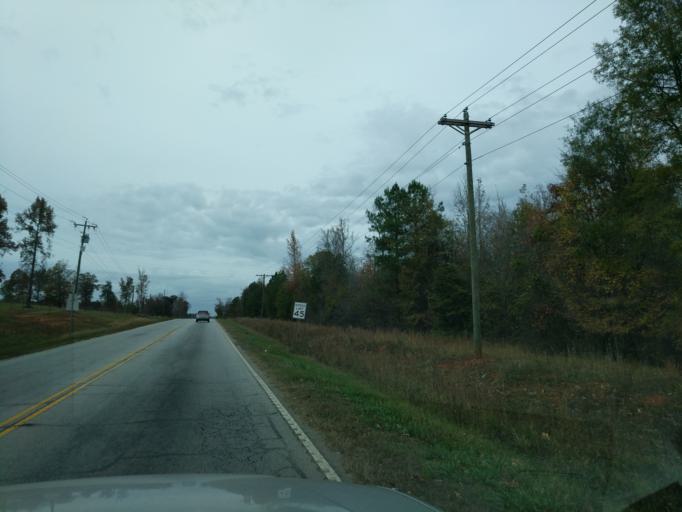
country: US
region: South Carolina
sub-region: Newberry County
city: Newberry
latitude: 34.2542
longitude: -81.6389
